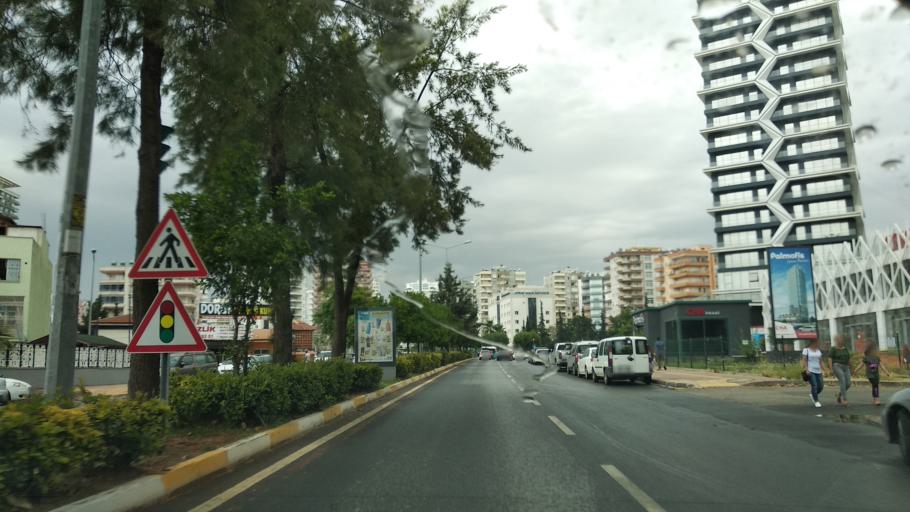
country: TR
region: Mersin
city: Mercin
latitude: 36.7871
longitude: 34.5885
